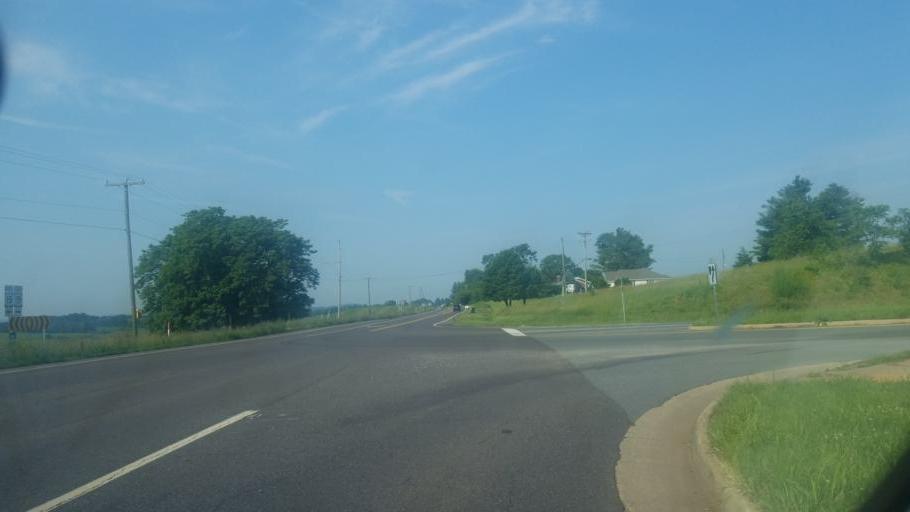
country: US
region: Virginia
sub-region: Culpeper County
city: Culpeper
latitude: 38.4408
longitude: -78.0207
